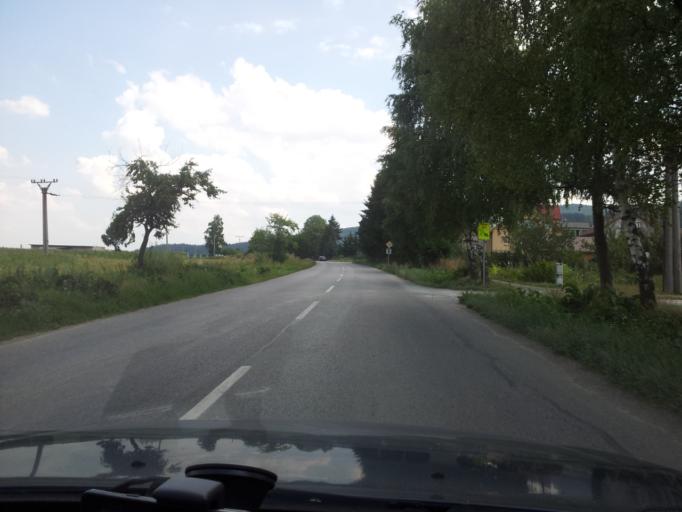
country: SK
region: Zilinsky
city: Namestovo
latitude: 49.3888
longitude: 19.4645
